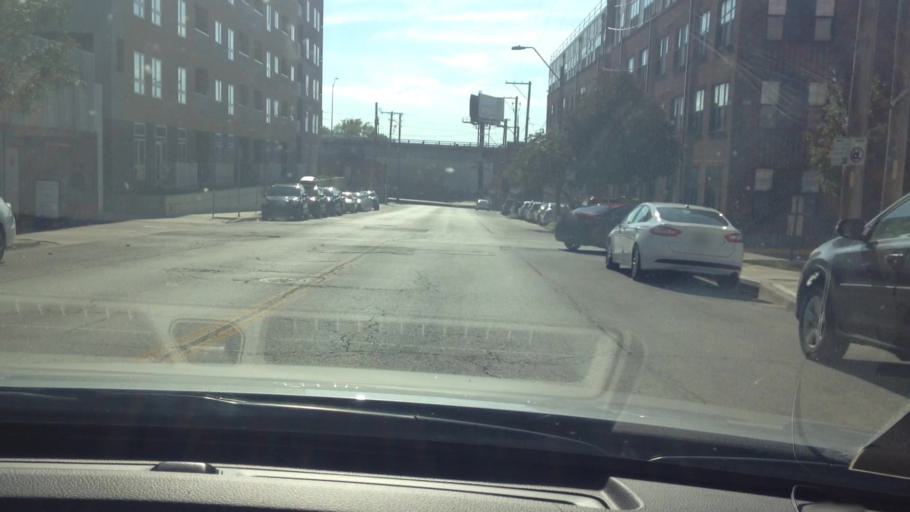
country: US
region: Missouri
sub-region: Jackson County
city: Kansas City
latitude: 39.1093
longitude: -94.5865
